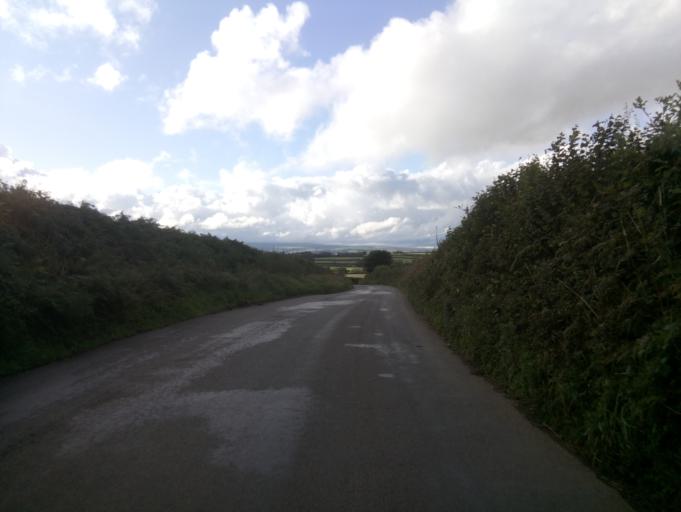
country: GB
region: England
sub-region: Devon
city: South Brent
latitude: 50.3826
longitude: -3.7664
